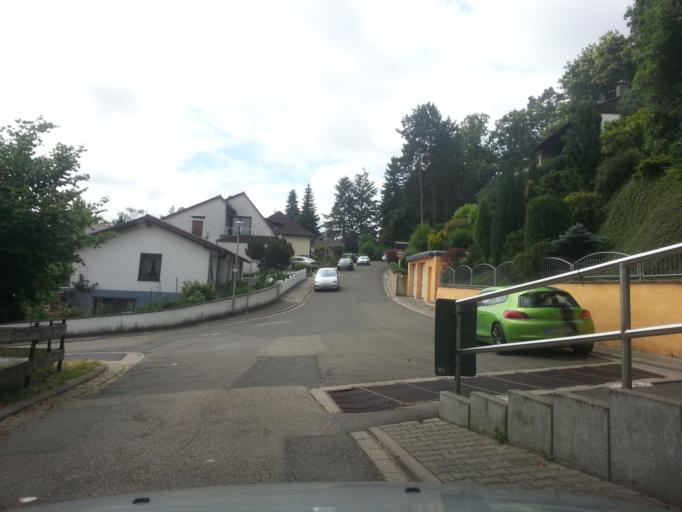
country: DE
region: Rheinland-Pfalz
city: Weisenheim am Berg
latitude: 49.5144
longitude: 8.1465
